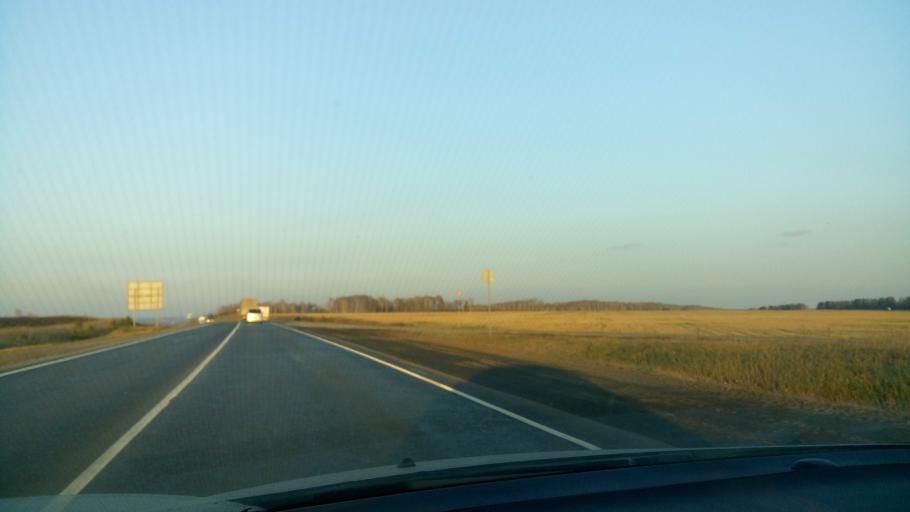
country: RU
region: Sverdlovsk
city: Yelanskiy
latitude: 56.7866
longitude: 62.5037
